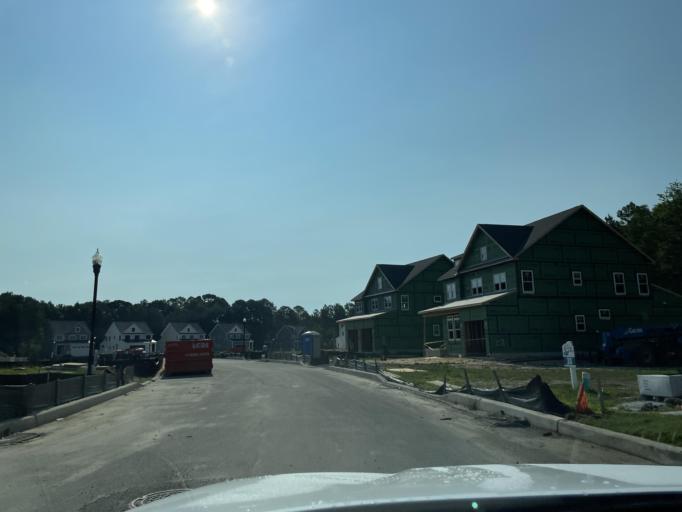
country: US
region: Delaware
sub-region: Sussex County
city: Ocean View
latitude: 38.5455
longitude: -75.0854
